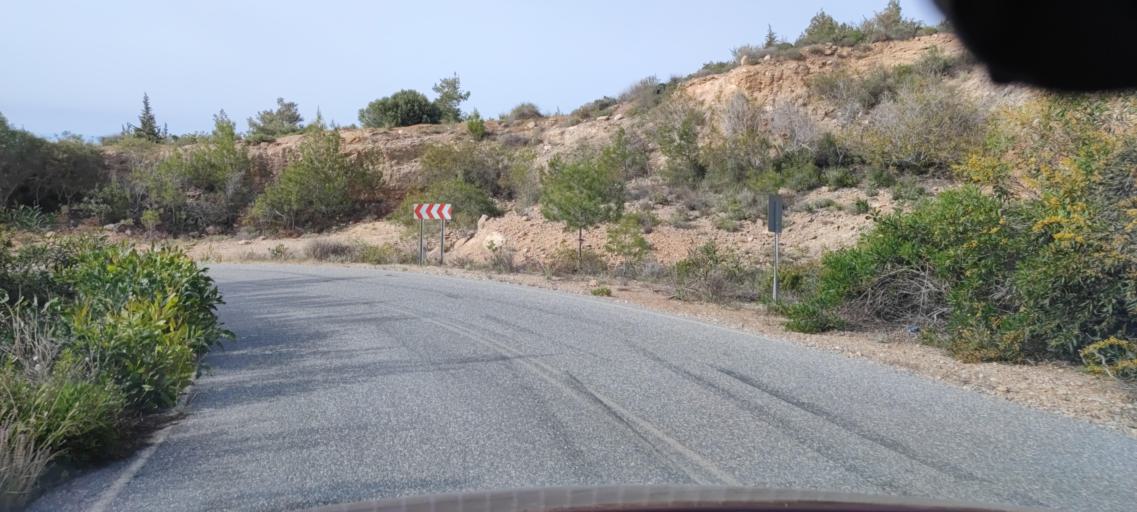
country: CY
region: Ammochostos
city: Trikomo
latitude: 35.4097
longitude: 33.9053
